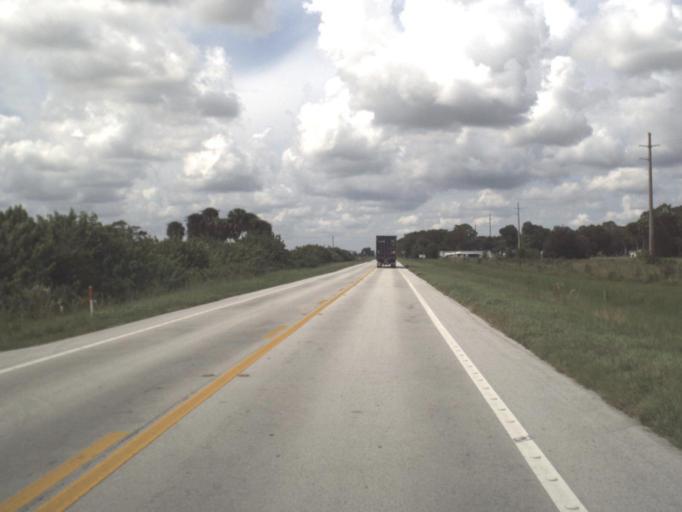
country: US
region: Florida
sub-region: Glades County
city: Buckhead Ridge
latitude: 27.2363
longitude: -81.0008
